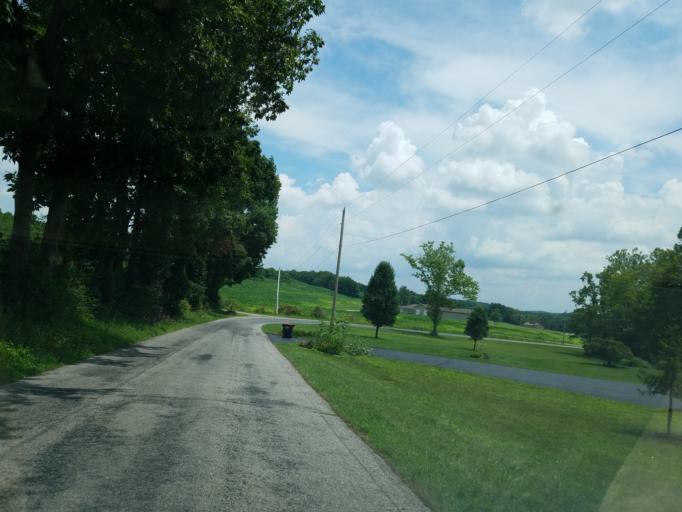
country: US
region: Ohio
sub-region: Licking County
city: Newark
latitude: 40.1312
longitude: -82.4127
